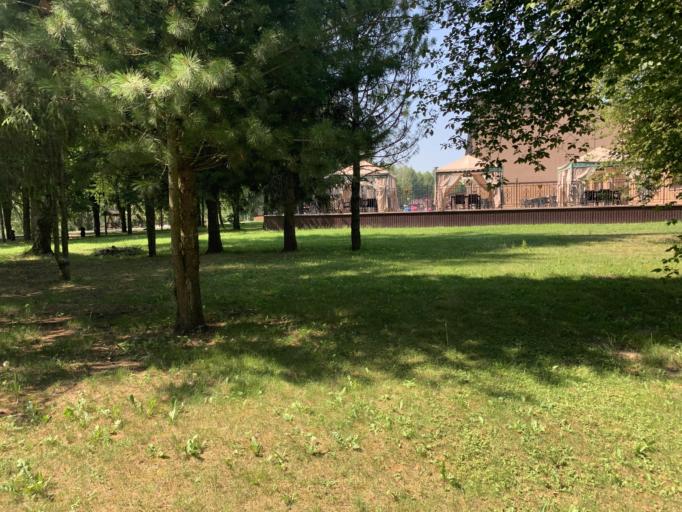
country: RU
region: Kostroma
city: Oktyabr'skiy
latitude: 57.6409
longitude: 41.0935
